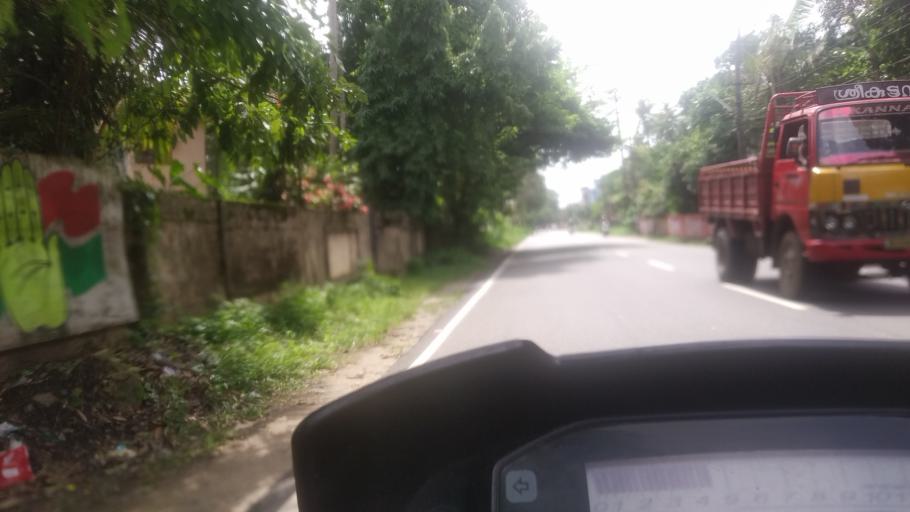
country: IN
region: Kerala
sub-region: Ernakulam
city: Elur
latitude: 10.1395
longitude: 76.2656
